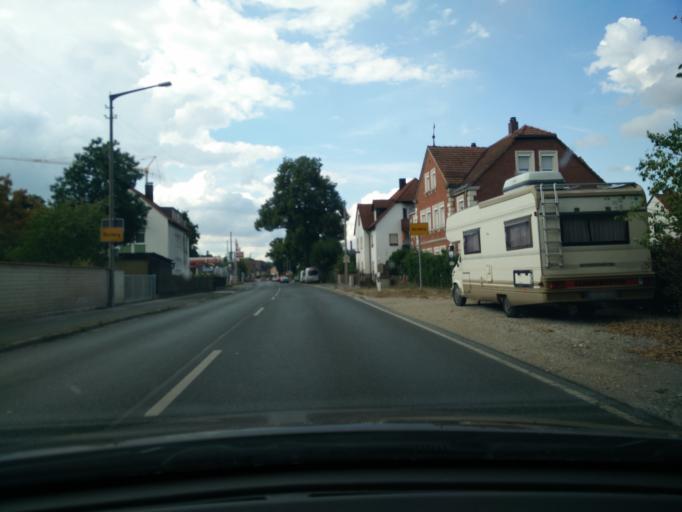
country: DE
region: Bavaria
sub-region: Regierungsbezirk Mittelfranken
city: Schwabach
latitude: 49.3724
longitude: 11.0268
